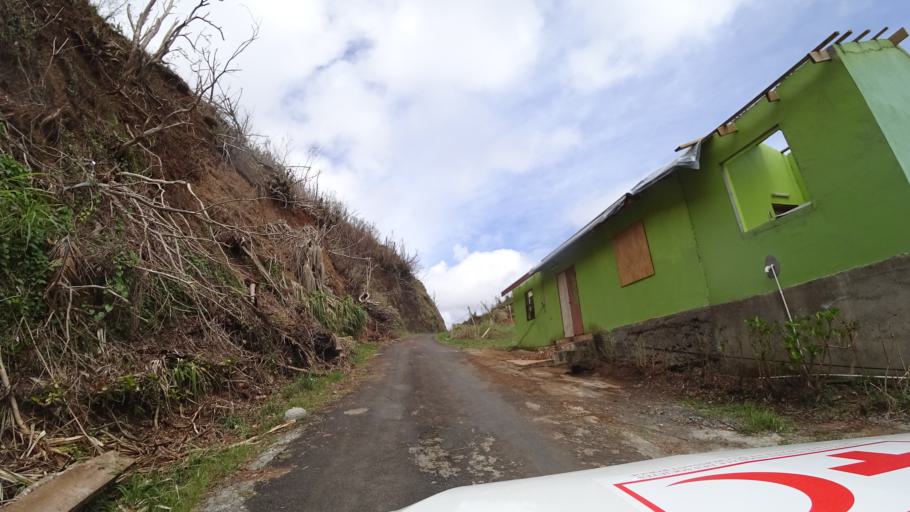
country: DM
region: Saint David
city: Rosalie
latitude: 15.3920
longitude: -61.2588
